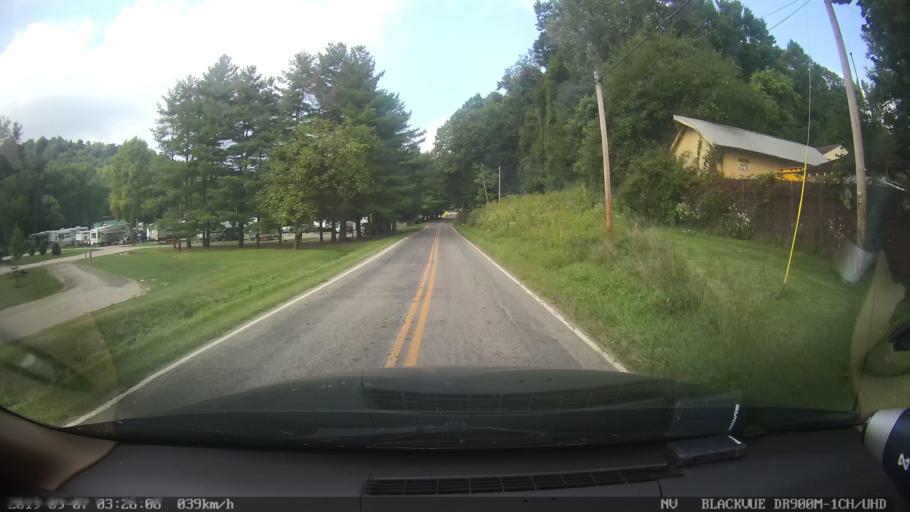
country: US
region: Ohio
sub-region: Licking County
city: Granville
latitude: 40.1236
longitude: -82.4912
